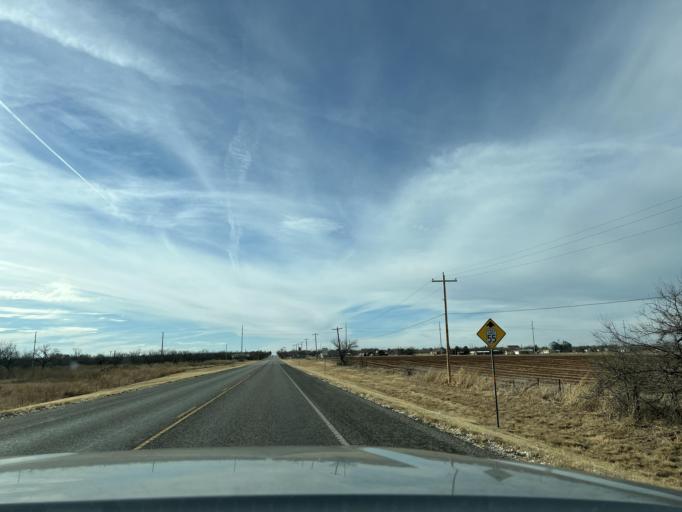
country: US
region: Texas
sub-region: Jones County
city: Anson
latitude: 32.7515
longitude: -99.8830
